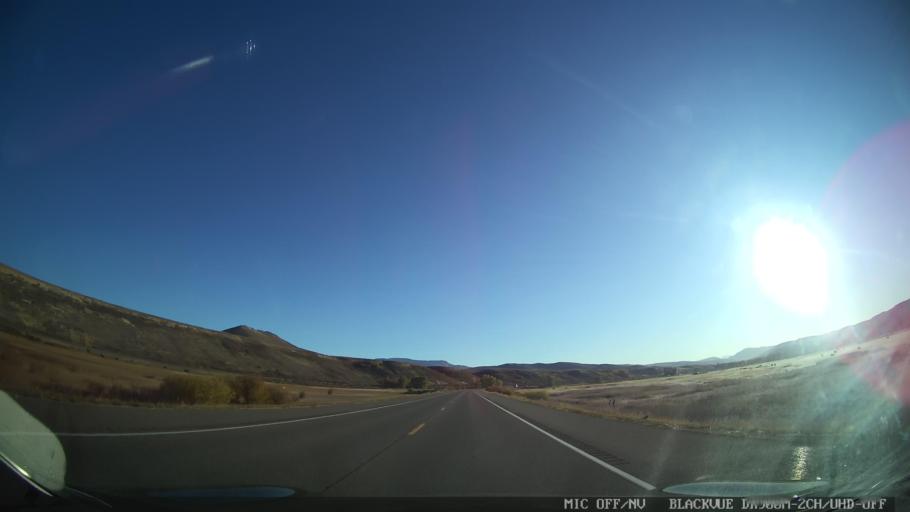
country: US
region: Colorado
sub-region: Grand County
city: Kremmling
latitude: 40.0655
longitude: -106.2763
